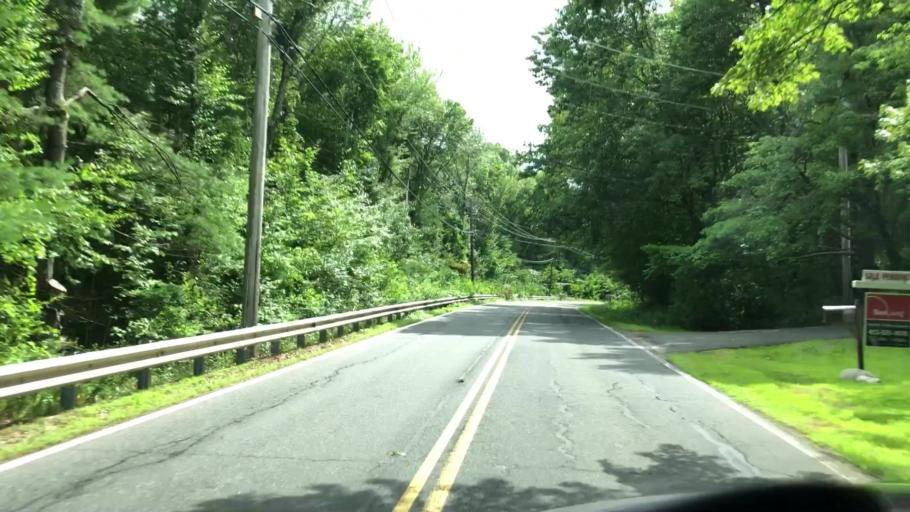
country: US
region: Massachusetts
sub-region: Hampden County
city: Holyoke
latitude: 42.2182
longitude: -72.6609
